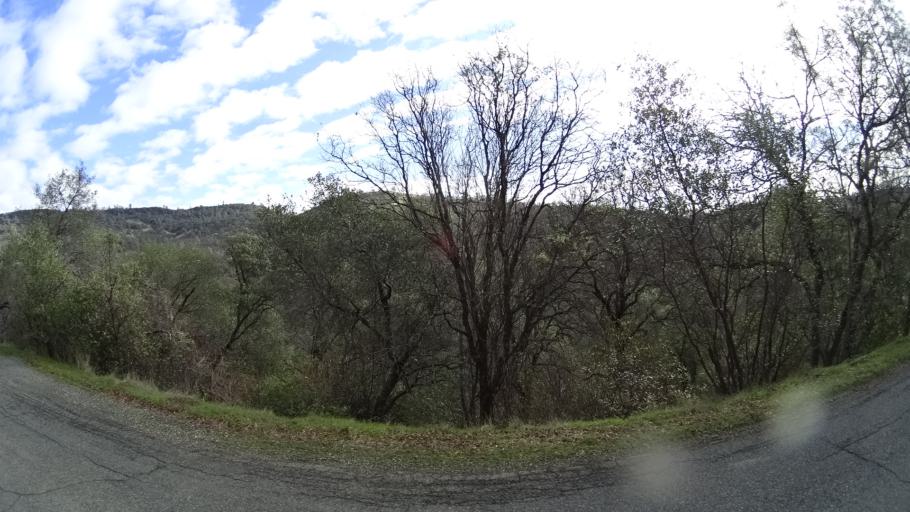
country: US
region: California
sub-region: Butte County
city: Oroville
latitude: 39.5523
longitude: -121.5407
